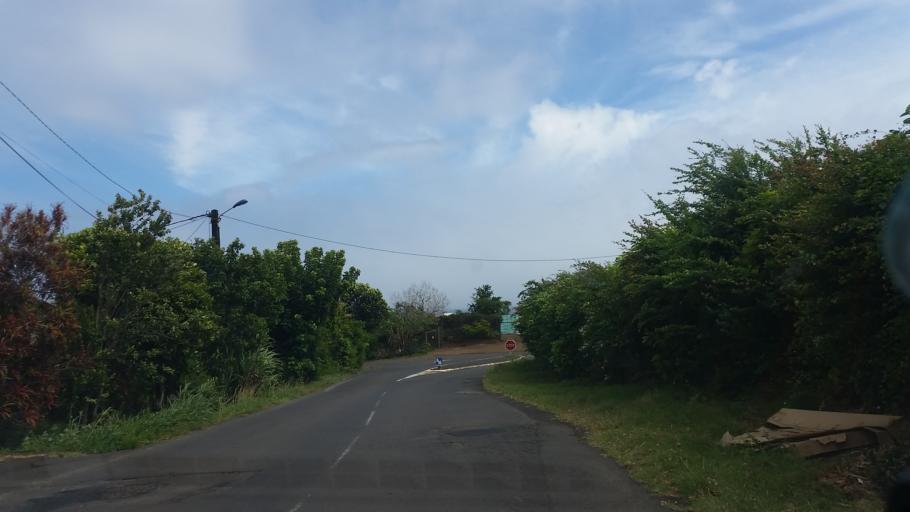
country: RE
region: Reunion
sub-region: Reunion
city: Sainte-Marie
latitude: -20.9155
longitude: 55.5329
